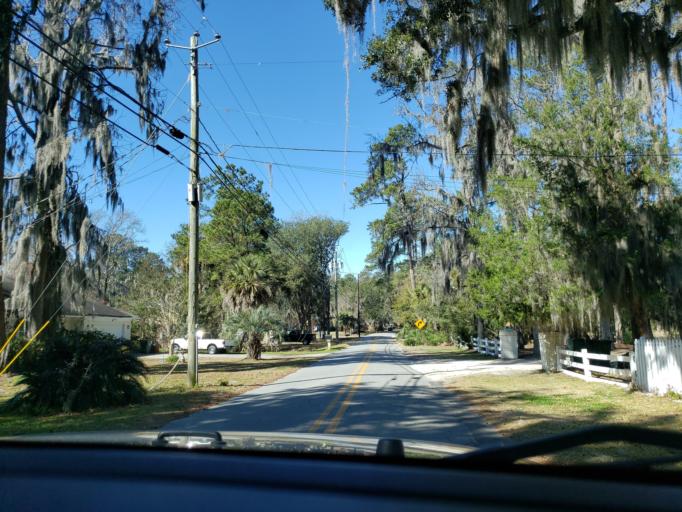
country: US
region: Georgia
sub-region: Chatham County
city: Whitemarsh Island
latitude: 32.0417
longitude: -80.9943
